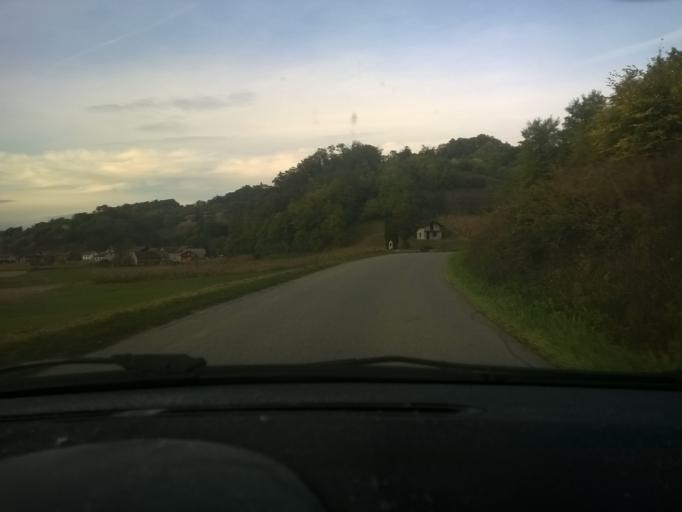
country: HR
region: Krapinsko-Zagorska
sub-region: Grad Krapina
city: Krapina
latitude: 46.0930
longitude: 15.8815
